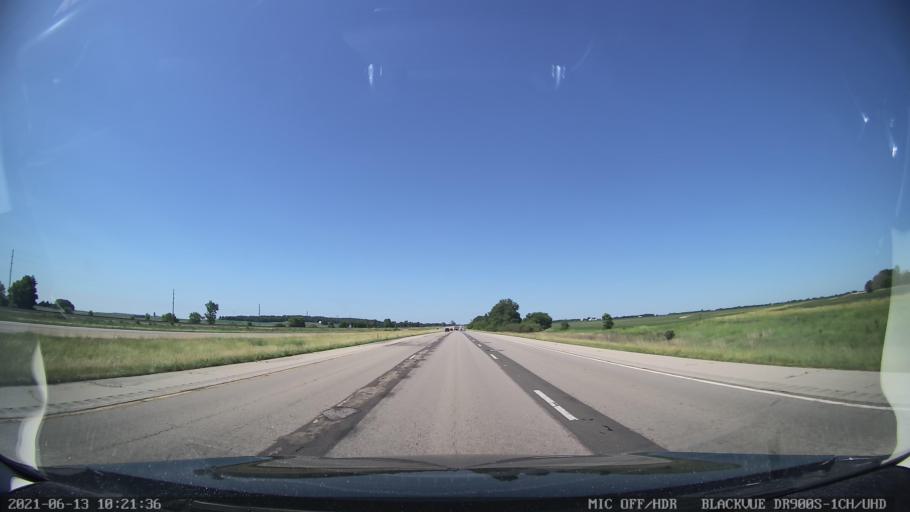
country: US
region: Illinois
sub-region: Sangamon County
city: Williamsville
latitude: 40.0498
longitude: -89.4598
